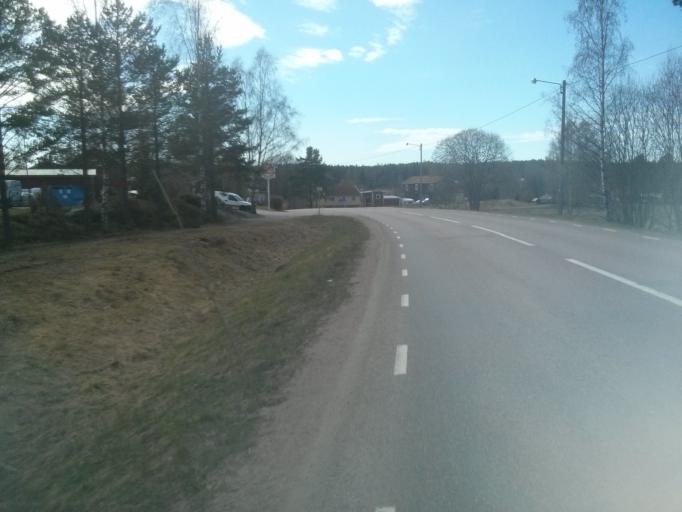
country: SE
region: Gaevleborg
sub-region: Hudiksvalls Kommun
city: Hudiksvall
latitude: 61.8337
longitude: 17.2572
